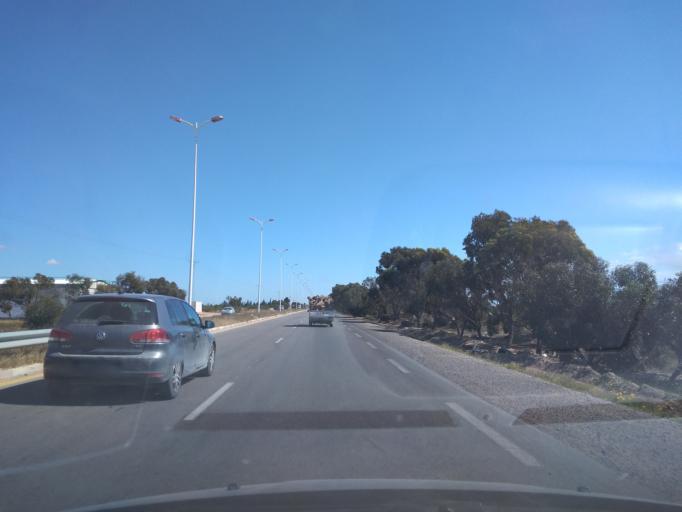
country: TN
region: Safaqis
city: Sfax
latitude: 34.8280
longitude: 10.7200
